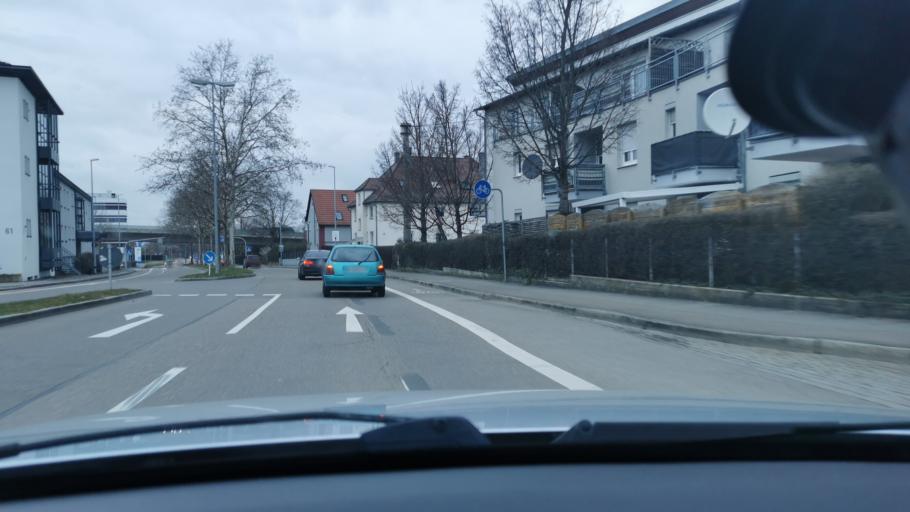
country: DE
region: Baden-Wuerttemberg
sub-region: Regierungsbezirk Stuttgart
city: Kirchheim unter Teck
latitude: 48.6454
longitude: 9.4437
